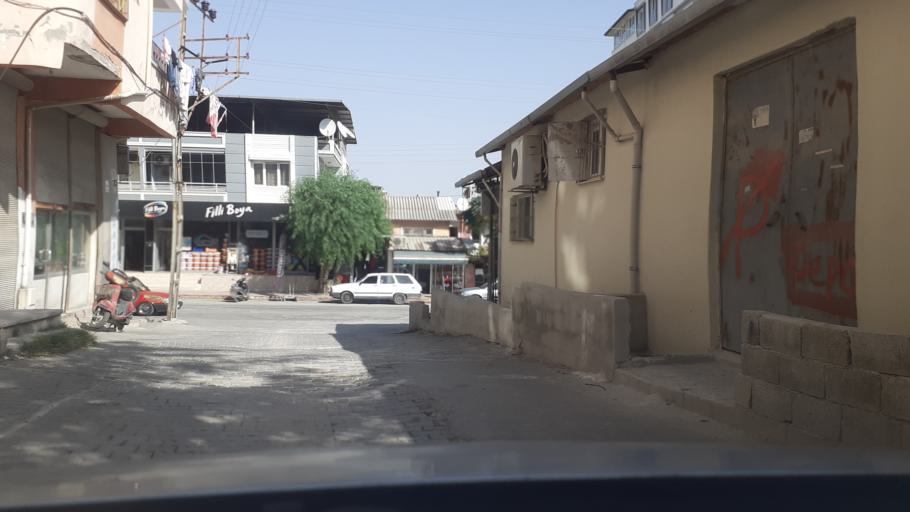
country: TR
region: Hatay
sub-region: Antakya Ilcesi
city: Antakya
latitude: 36.2116
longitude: 36.1522
